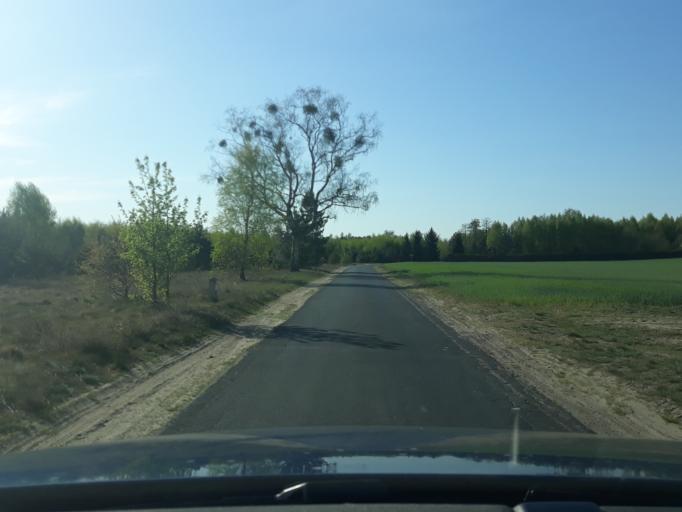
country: PL
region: Pomeranian Voivodeship
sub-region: Powiat czluchowski
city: Przechlewo
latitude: 53.8773
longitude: 17.3254
